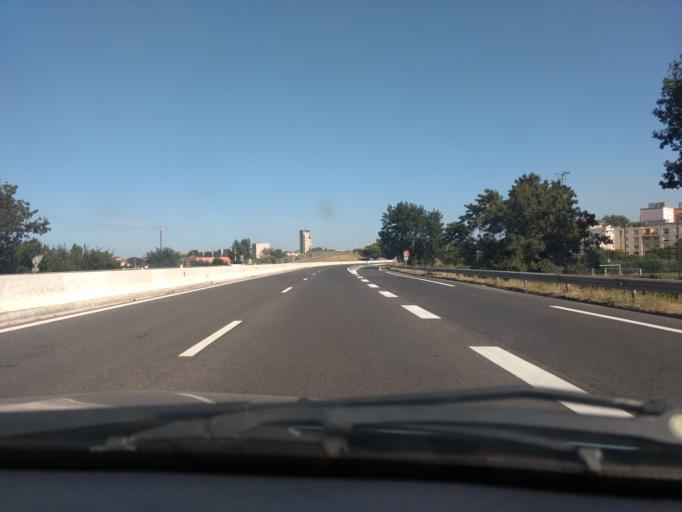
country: FR
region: Languedoc-Roussillon
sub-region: Departement des Pyrenees-Orientales
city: Perpignan
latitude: 42.7082
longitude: 2.8793
